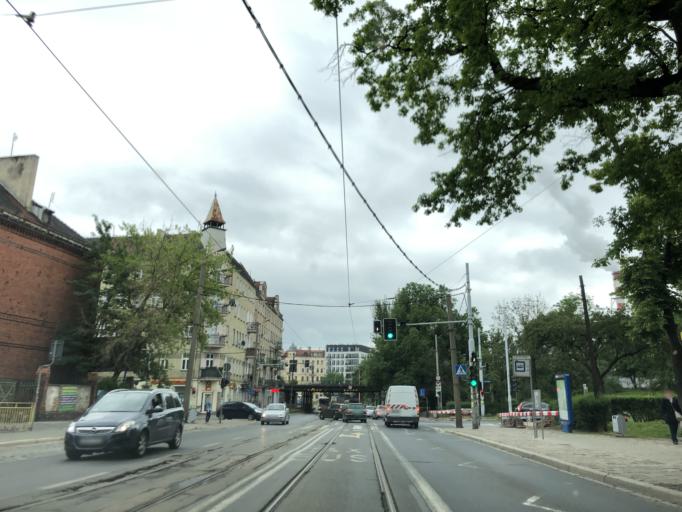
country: PL
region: Lower Silesian Voivodeship
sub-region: Powiat wroclawski
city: Wroclaw
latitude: 51.1275
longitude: 17.0276
